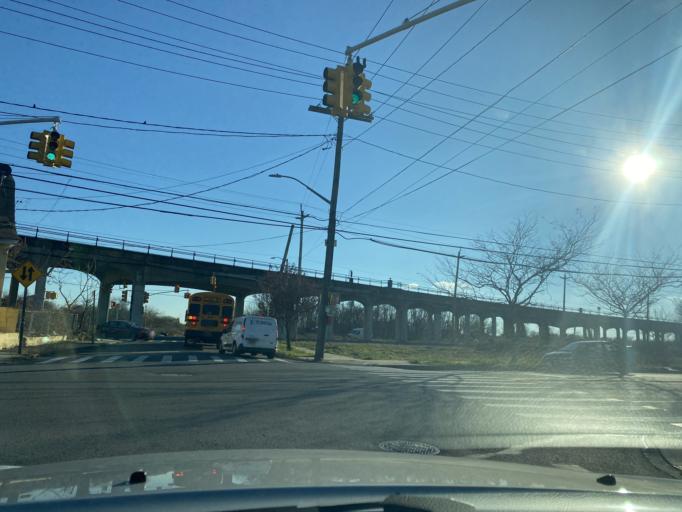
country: US
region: New York
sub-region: Nassau County
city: Inwood
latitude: 40.5947
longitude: -73.7704
